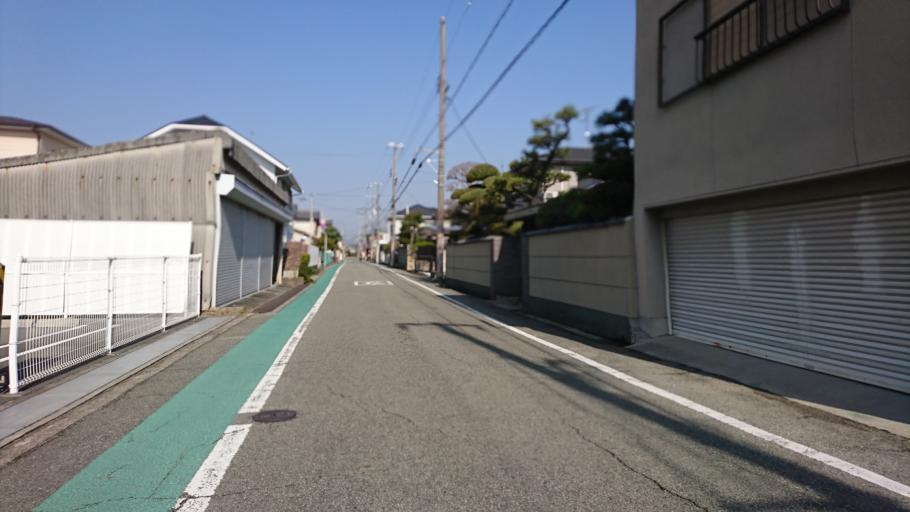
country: JP
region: Hyogo
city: Kakogawacho-honmachi
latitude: 34.7653
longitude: 134.8296
